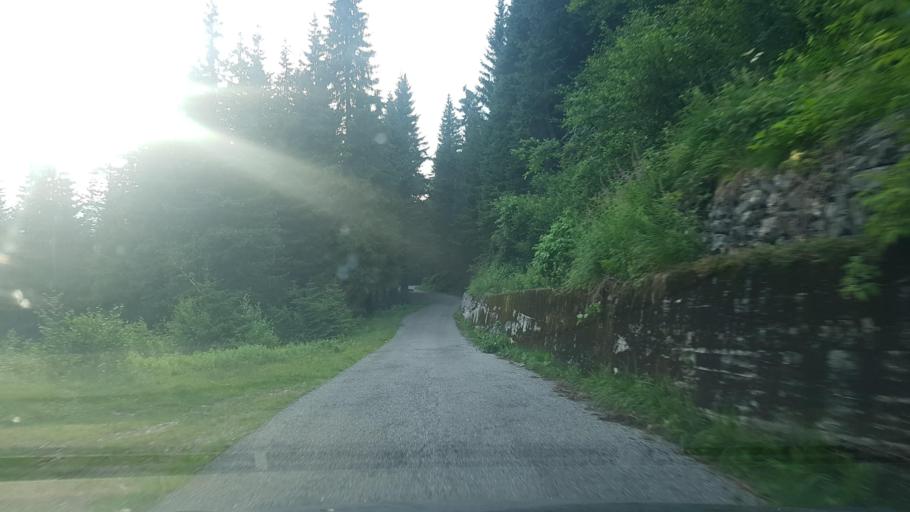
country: IT
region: Friuli Venezia Giulia
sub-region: Provincia di Udine
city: Paularo
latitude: 46.5693
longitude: 13.1666
